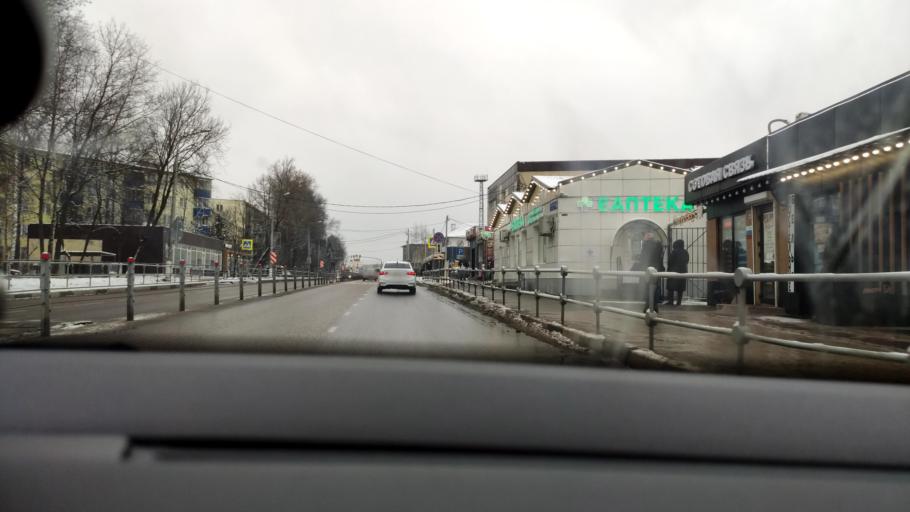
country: RU
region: Moskovskaya
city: Solnechnogorsk
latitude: 56.1862
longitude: 36.9711
